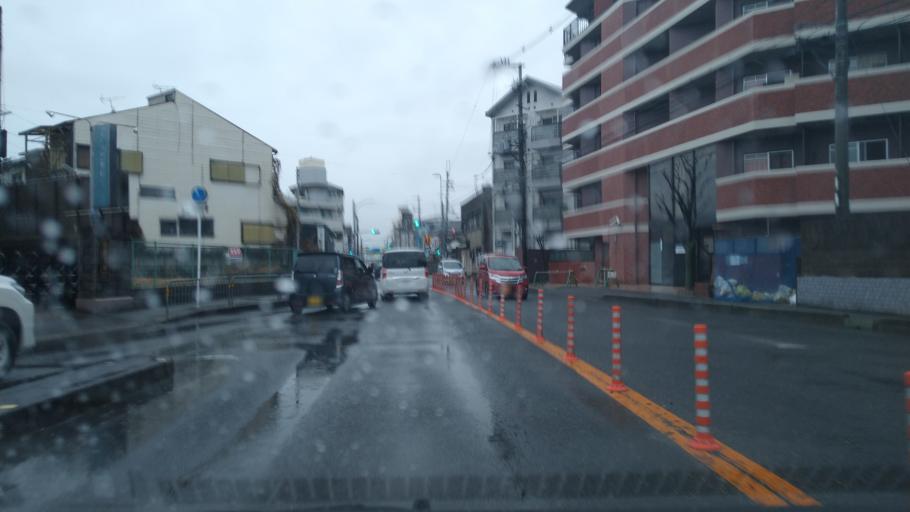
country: JP
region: Kyoto
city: Uji
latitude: 34.9238
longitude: 135.7709
